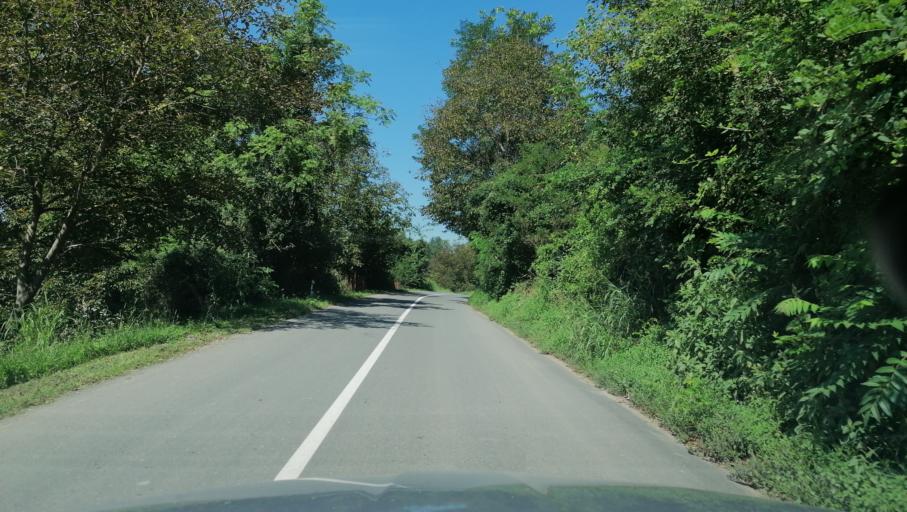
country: RS
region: Central Serbia
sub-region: Raski Okrug
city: Vrnjacka Banja
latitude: 43.6606
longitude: 20.9287
